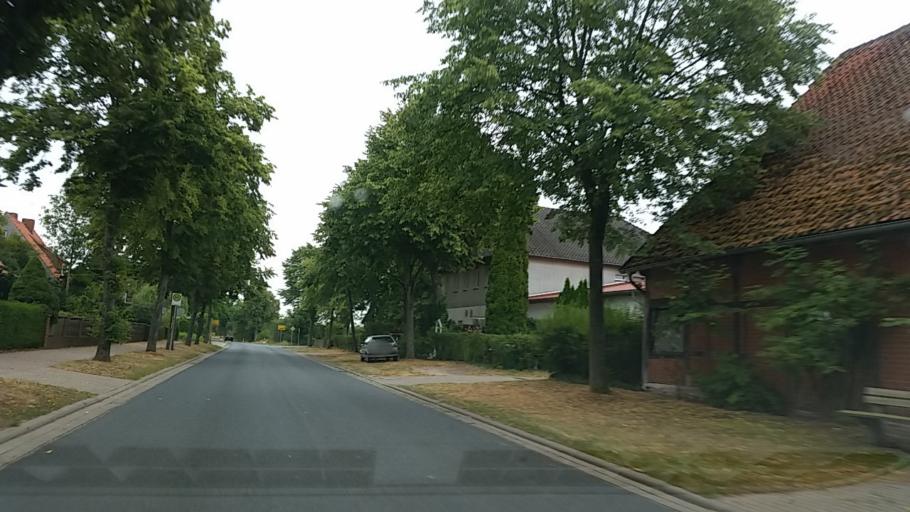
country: DE
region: Lower Saxony
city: Gilten
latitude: 52.7078
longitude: 9.5793
